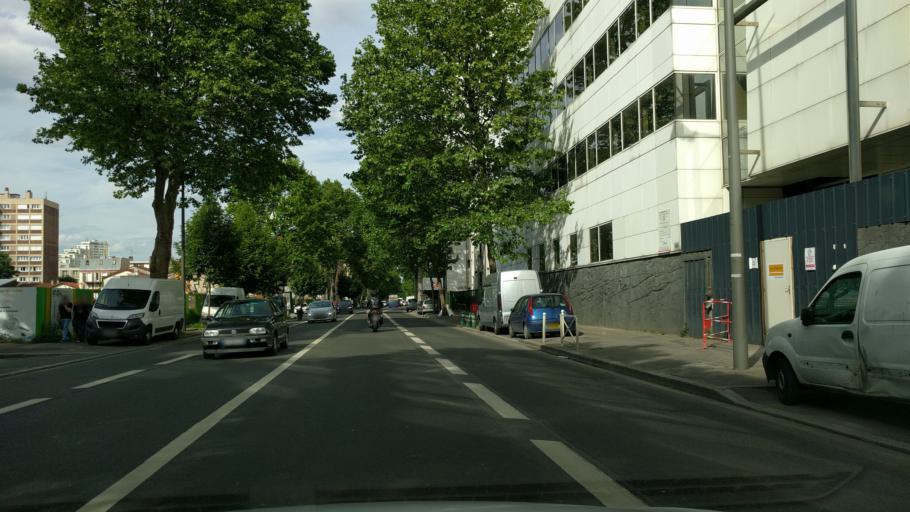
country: FR
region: Ile-de-France
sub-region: Departement des Hauts-de-Seine
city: Malakoff
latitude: 48.8146
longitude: 2.3038
